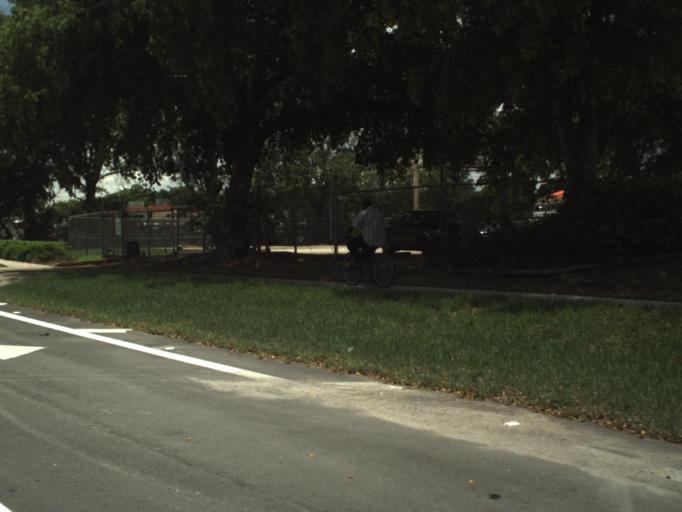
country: US
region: Florida
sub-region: Broward County
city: Wilton Manors
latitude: 26.1639
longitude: -80.1317
